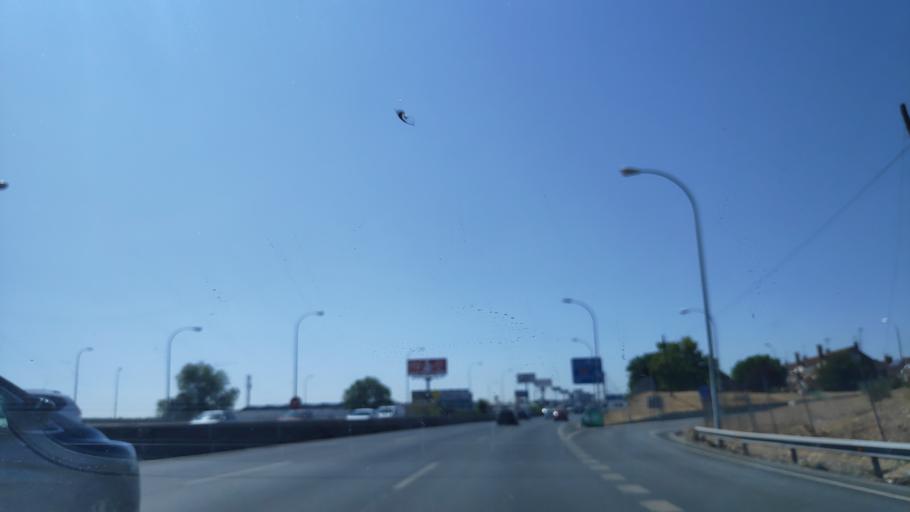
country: ES
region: Madrid
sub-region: Provincia de Madrid
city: Getafe
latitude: 40.2956
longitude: -3.7379
